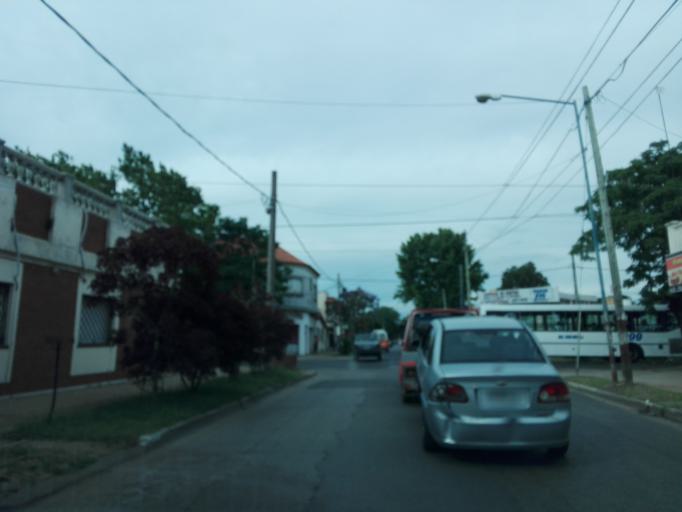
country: AR
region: Buenos Aires
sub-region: Partido de Lanus
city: Lanus
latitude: -34.7188
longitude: -58.3815
